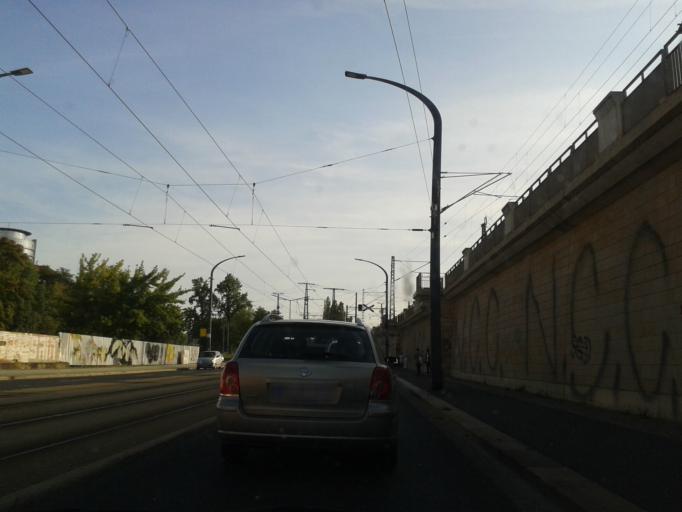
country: DE
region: Saxony
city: Dresden
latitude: 51.0525
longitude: 13.7208
